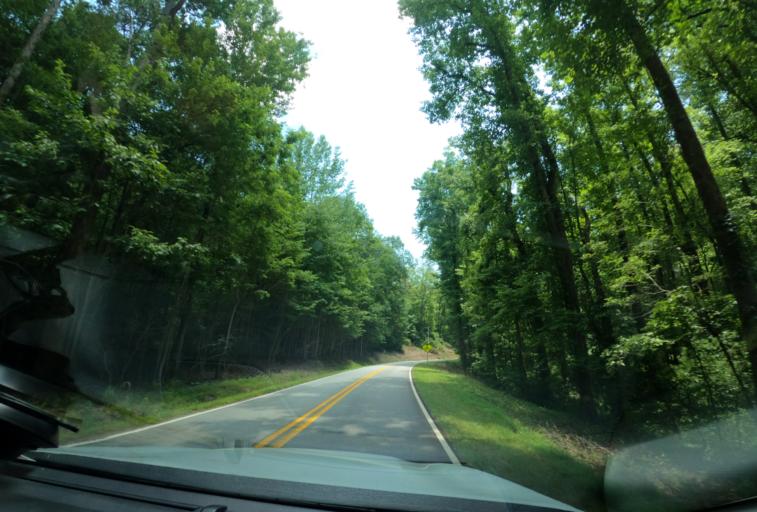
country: US
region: South Carolina
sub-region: Pickens County
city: Pickens
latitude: 35.0050
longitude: -82.8129
